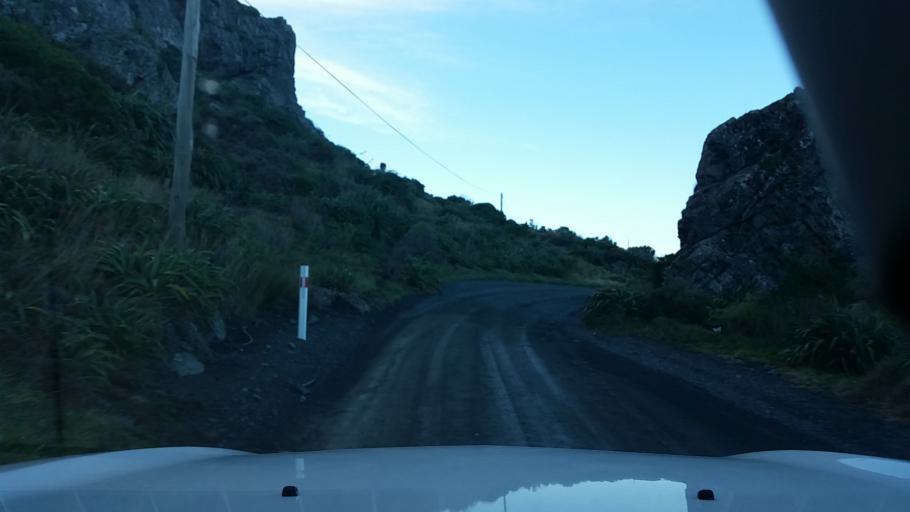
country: NZ
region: Wellington
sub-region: South Wairarapa District
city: Waipawa
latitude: -41.6081
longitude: 175.2722
